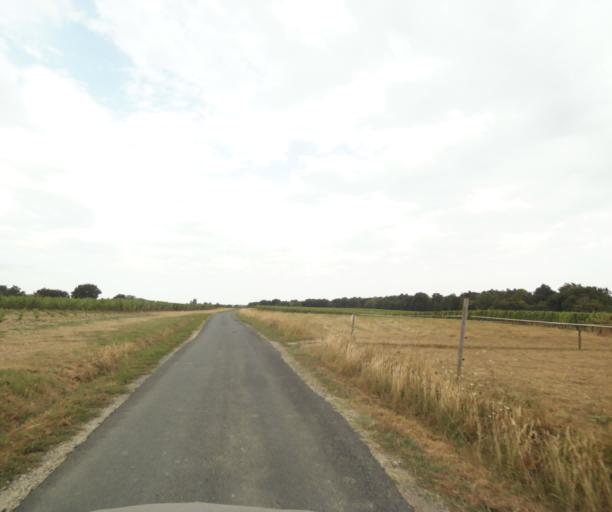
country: FR
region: Aquitaine
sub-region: Departement de la Gironde
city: Creon
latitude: 44.7513
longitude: -0.3388
